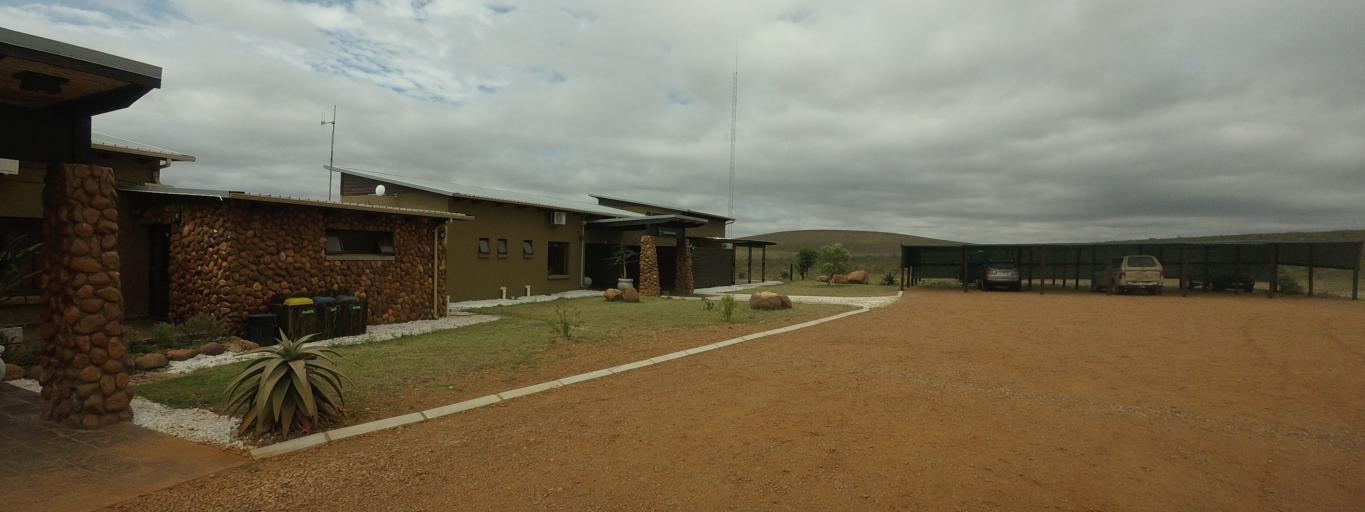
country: ZA
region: Western Cape
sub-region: Overberg District Municipality
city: Swellendam
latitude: -34.0592
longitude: 20.4307
